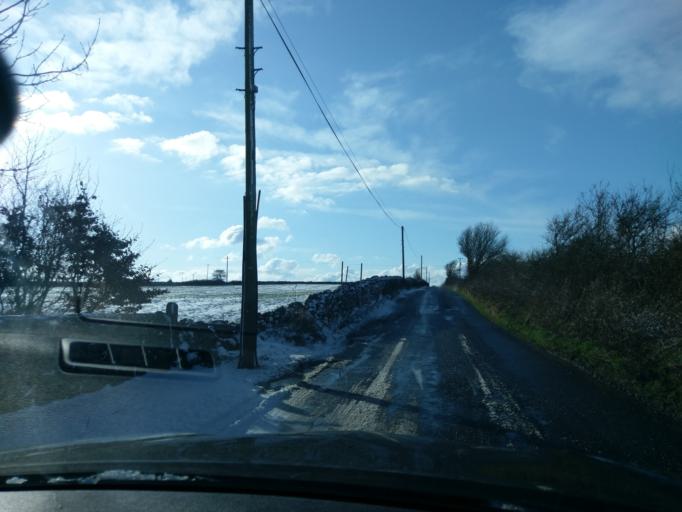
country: IE
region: Connaught
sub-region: County Galway
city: Oranmore
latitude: 53.2024
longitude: -8.8553
